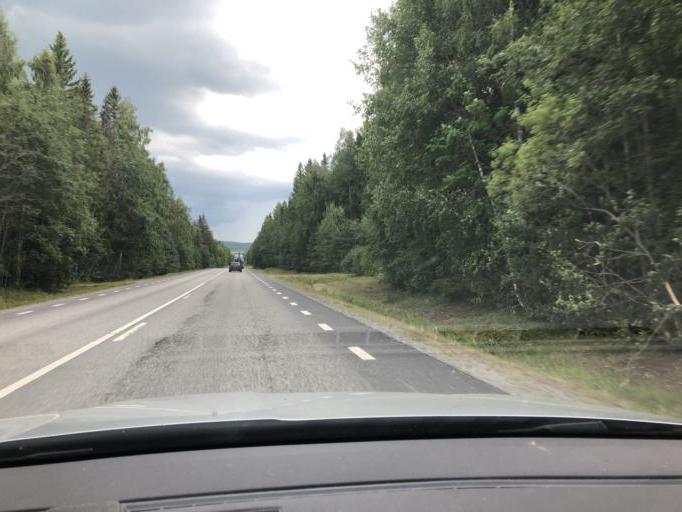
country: SE
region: Vaesternorrland
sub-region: Solleftea Kommun
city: Solleftea
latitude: 63.3059
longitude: 17.2030
